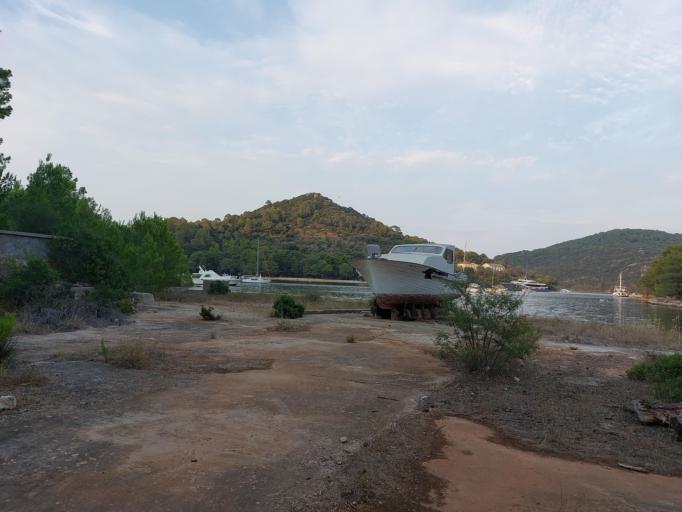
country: HR
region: Dubrovacko-Neretvanska
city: Smokvica
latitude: 42.7636
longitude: 16.8085
